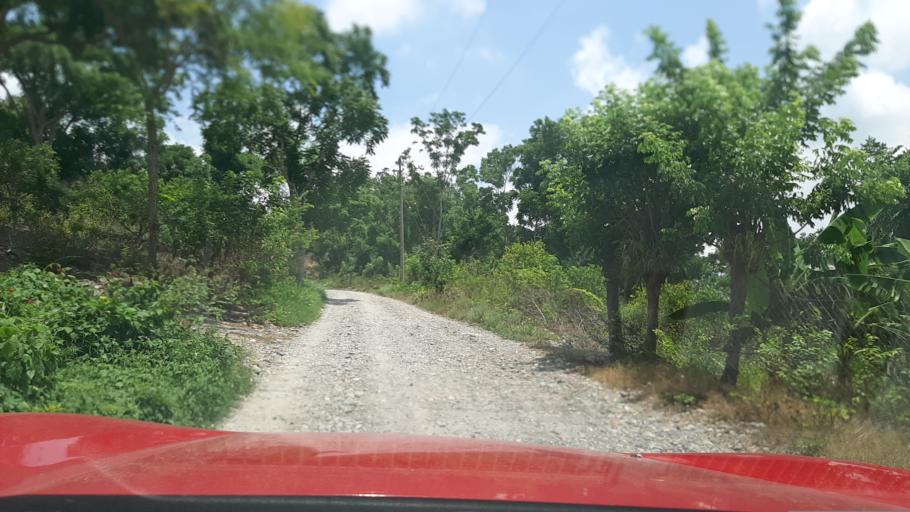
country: MX
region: Veracruz
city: Papantla de Olarte
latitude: 20.4296
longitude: -97.2643
